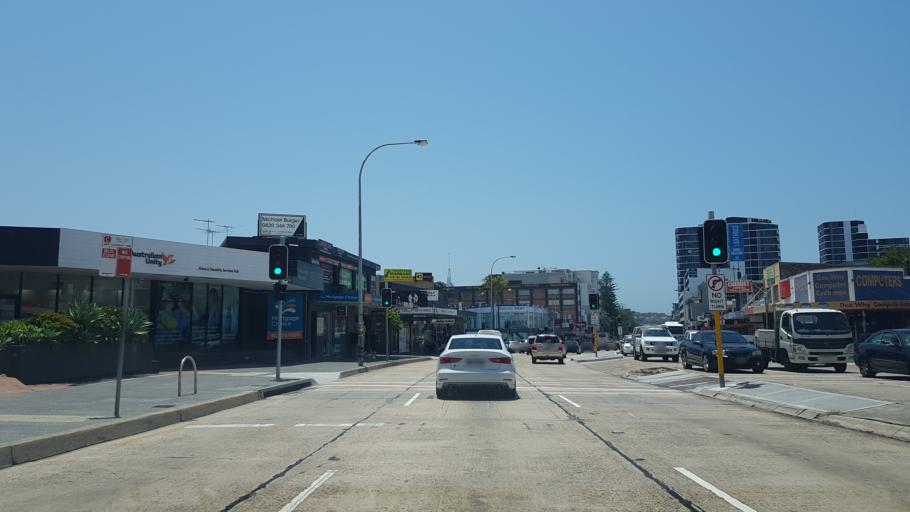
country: AU
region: New South Wales
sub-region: Warringah
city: Narraweena
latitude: -33.7546
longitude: 151.2840
